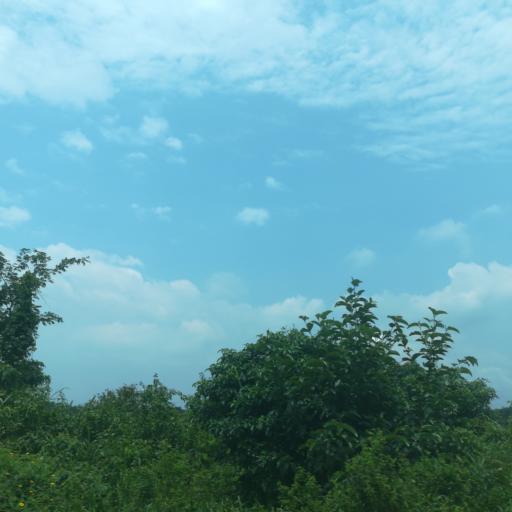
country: NG
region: Lagos
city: Ejirin
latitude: 6.6607
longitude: 3.8075
